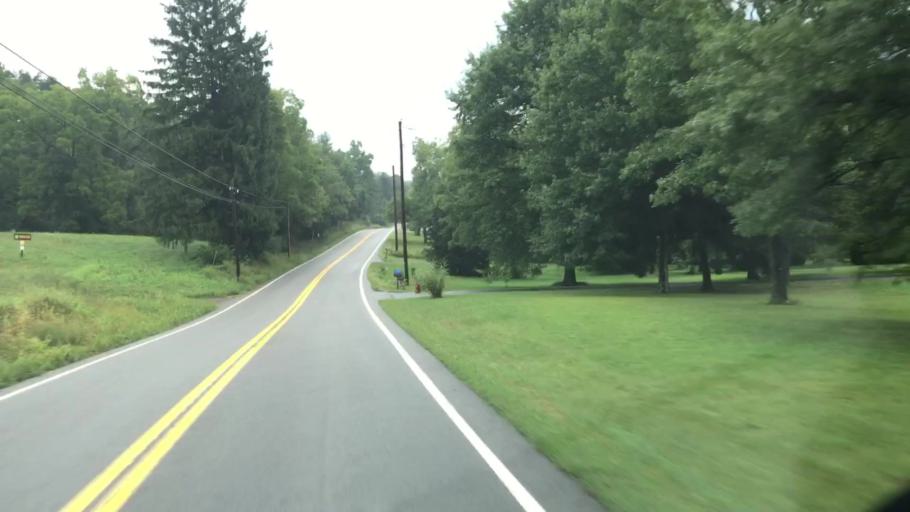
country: US
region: Pennsylvania
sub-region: Perry County
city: New Bloomfield
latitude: 40.3938
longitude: -77.1287
